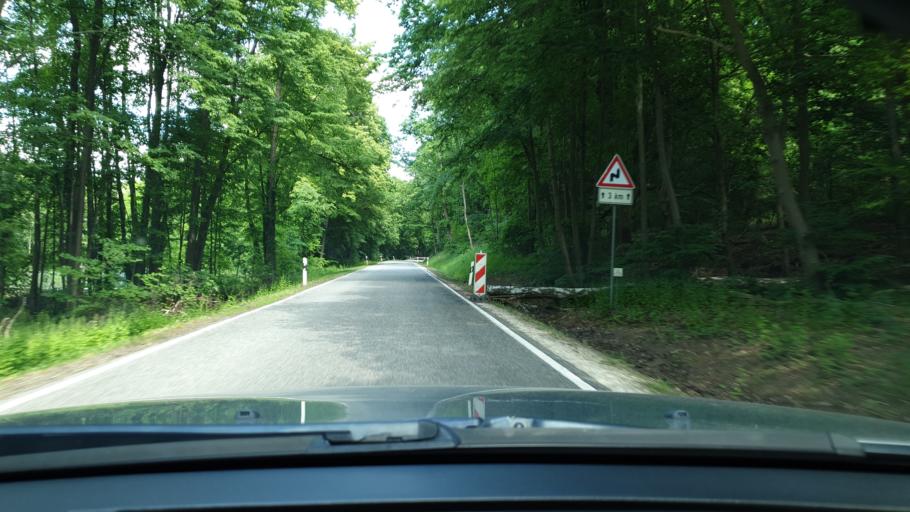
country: DE
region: Rheinland-Pfalz
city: Bechhofen
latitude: 49.3439
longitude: 7.3717
